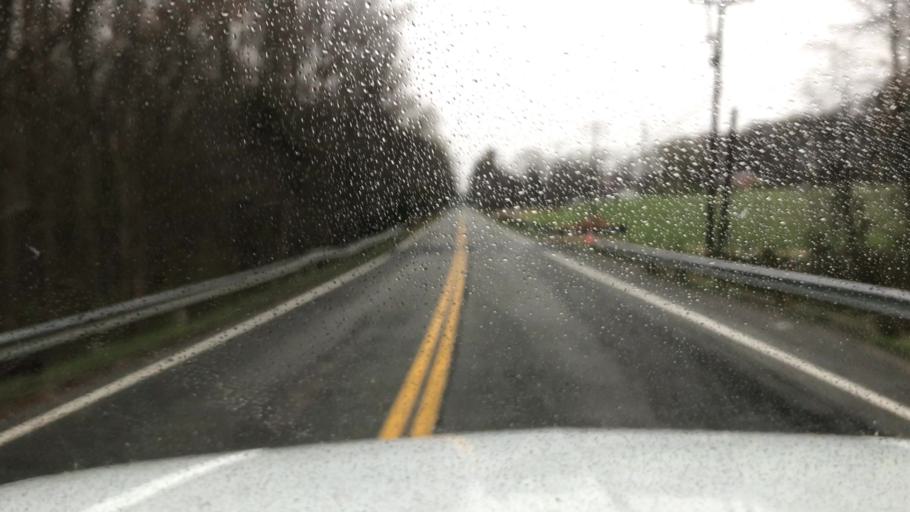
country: US
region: Virginia
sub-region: Henrico County
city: Short Pump
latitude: 37.6606
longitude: -77.6788
